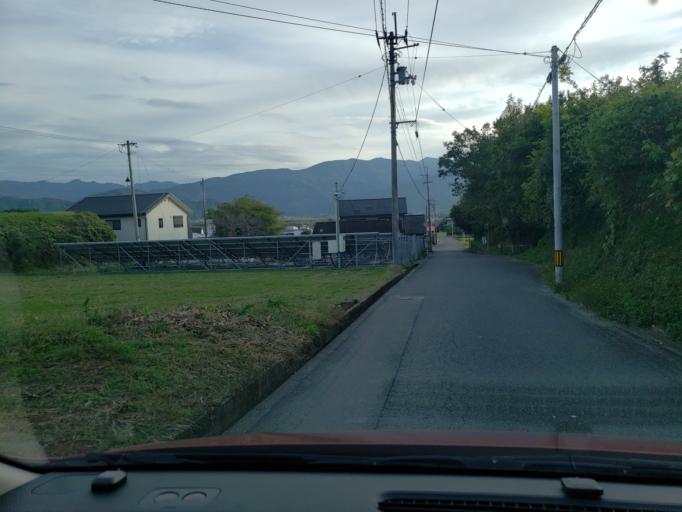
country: JP
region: Tokushima
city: Wakimachi
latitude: 34.0775
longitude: 134.2281
